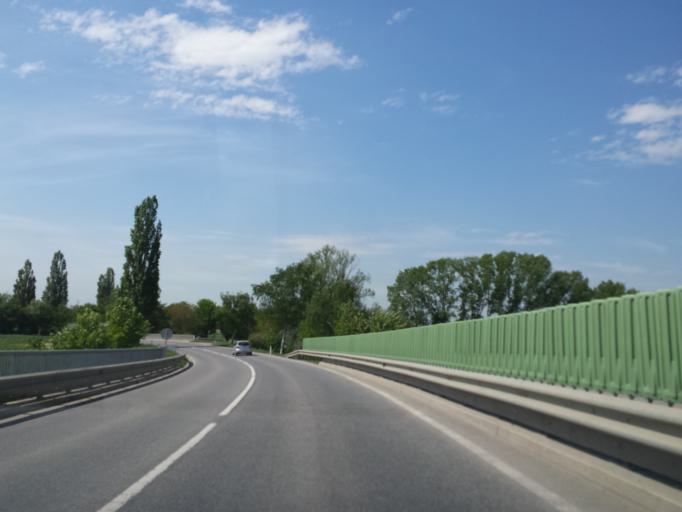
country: AT
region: Lower Austria
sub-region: Politischer Bezirk Tulln
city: Atzenbrugg
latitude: 48.2890
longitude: 15.9114
